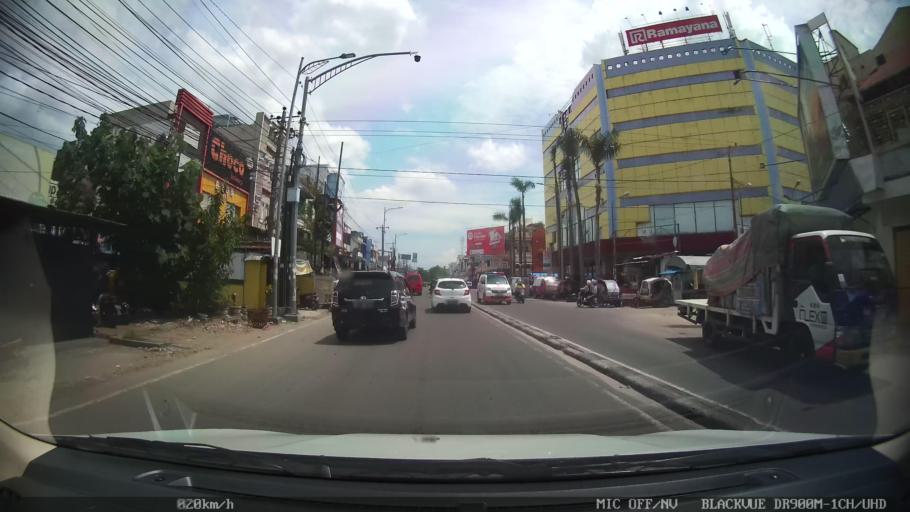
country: ID
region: North Sumatra
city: Medan
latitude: 3.5810
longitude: 98.6612
